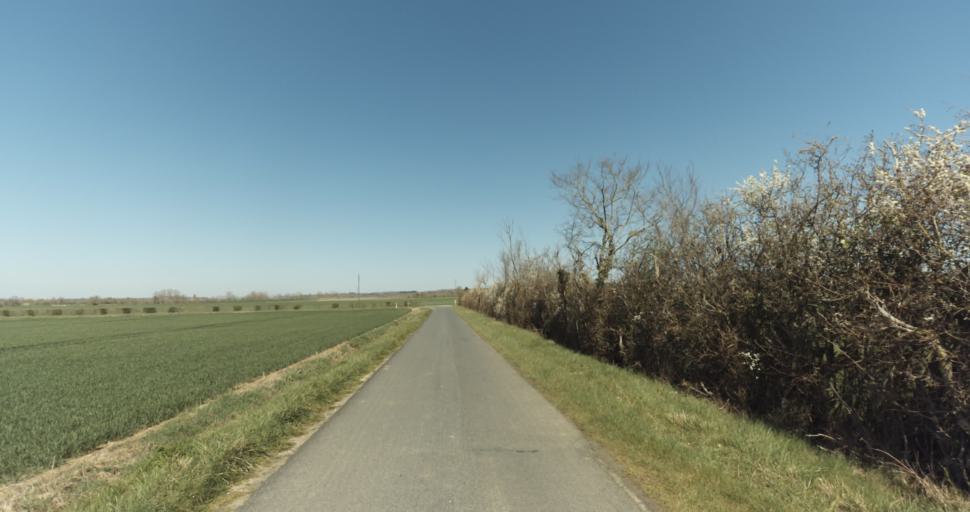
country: FR
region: Lower Normandy
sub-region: Departement du Calvados
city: Saint-Pierre-sur-Dives
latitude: 49.0171
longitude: 0.0295
